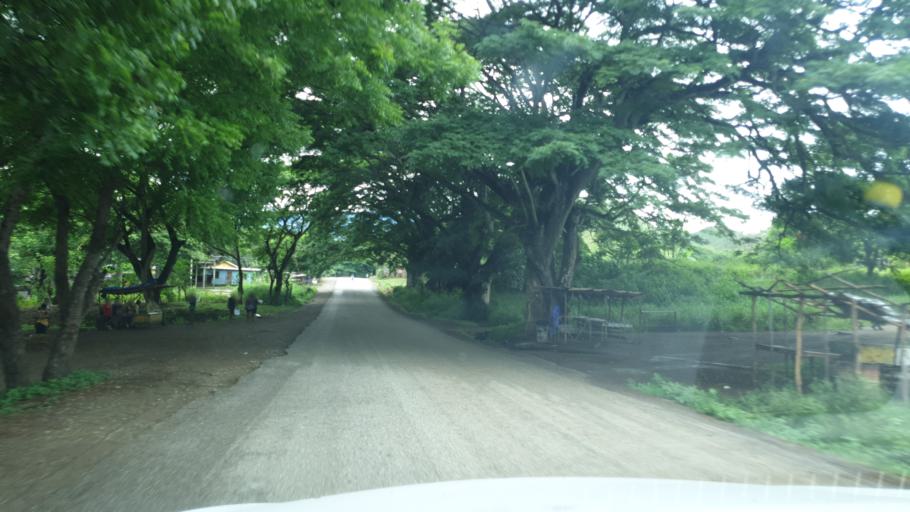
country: PG
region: National Capital
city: Port Moresby
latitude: -9.3923
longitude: 147.2860
